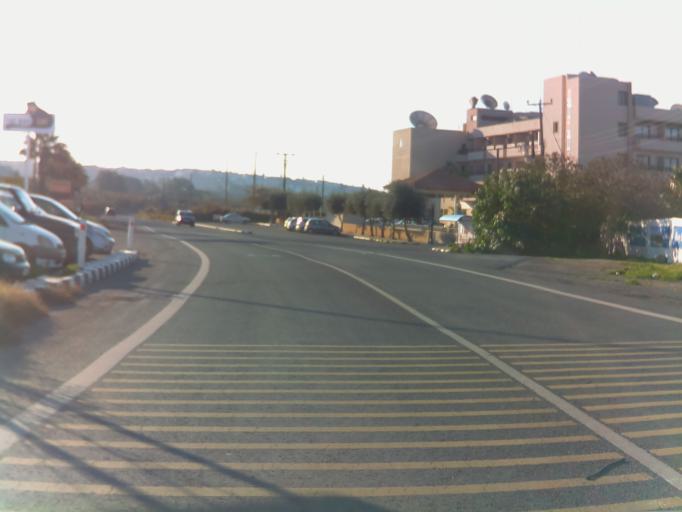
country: CY
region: Pafos
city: Kissonerga
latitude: 34.8228
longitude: 32.3926
